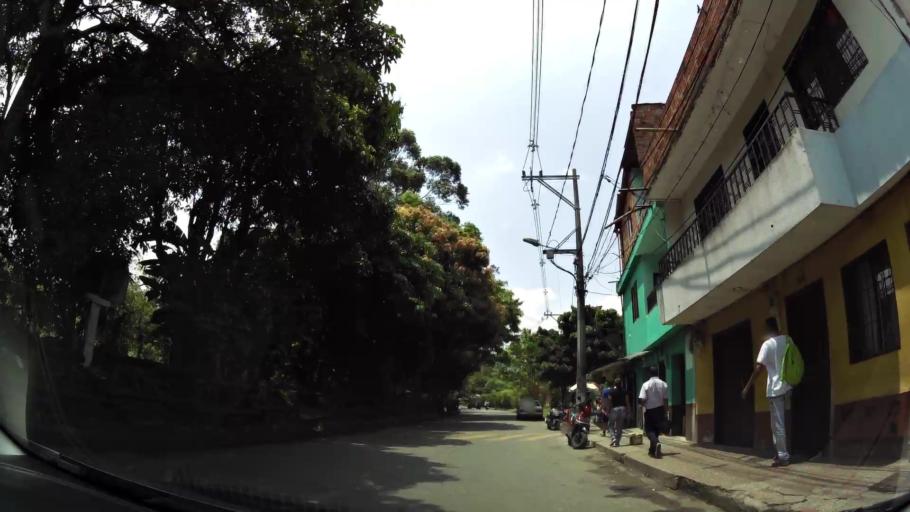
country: CO
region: Antioquia
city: Itagui
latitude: 6.1741
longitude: -75.6151
